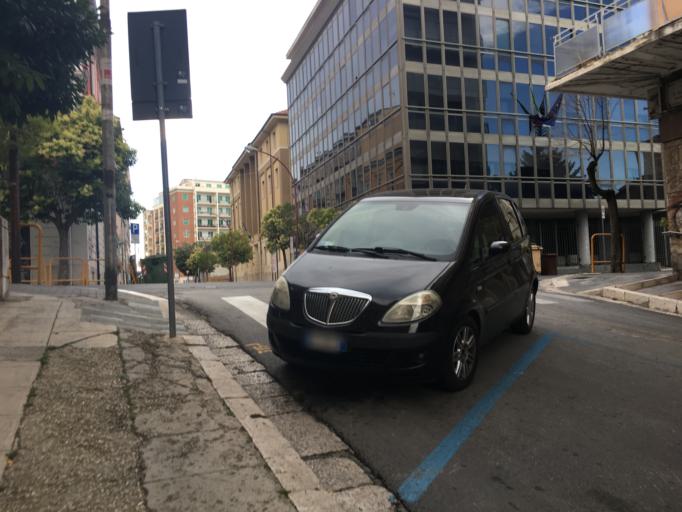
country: IT
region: Molise
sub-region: Provincia di Campobasso
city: Campobasso
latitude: 41.5557
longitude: 14.6588
